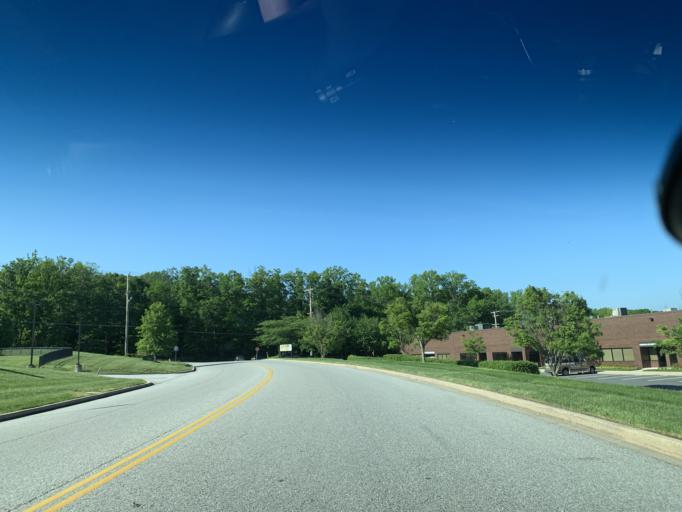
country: US
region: Maryland
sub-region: Harford County
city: Riverside
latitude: 39.4860
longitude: -76.2335
